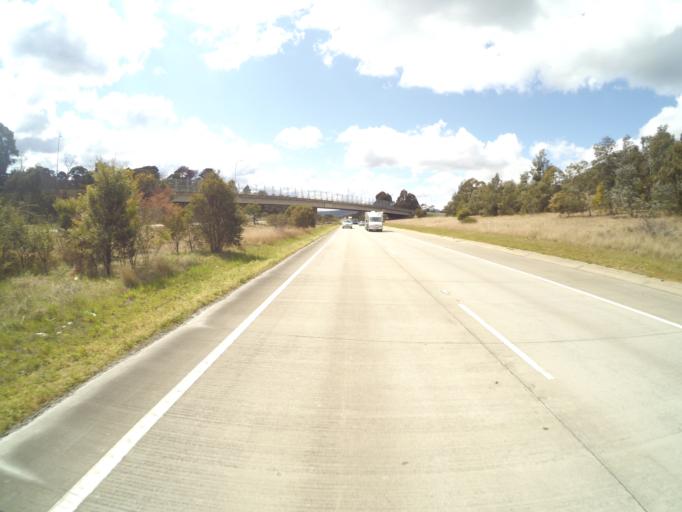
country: AU
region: New South Wales
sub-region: Wingecarribee
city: Mittagong
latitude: -34.4406
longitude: 150.4148
